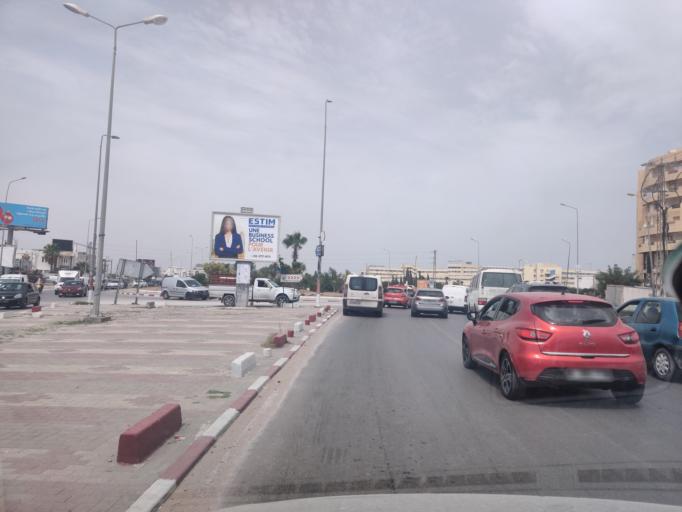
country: TN
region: Susah
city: Hammam Sousse
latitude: 35.8329
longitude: 10.5900
